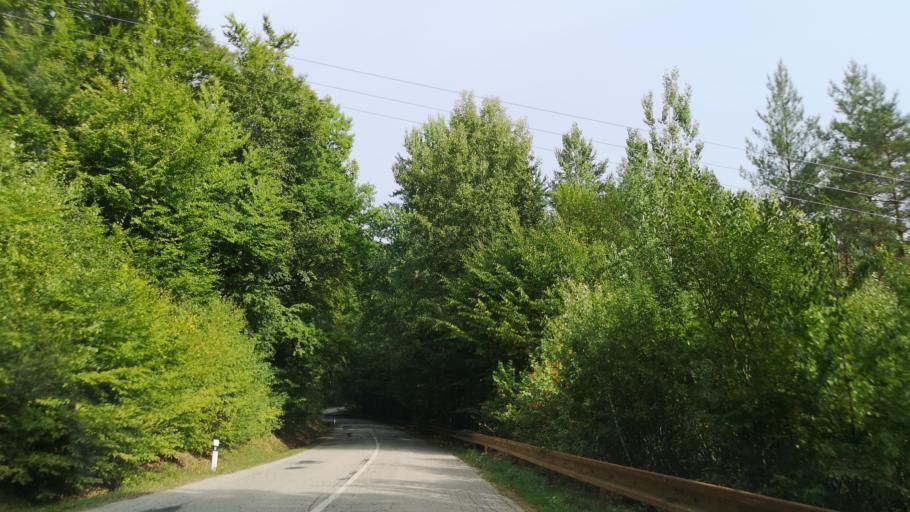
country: SK
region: Banskobystricky
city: Revuca
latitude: 48.6042
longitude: 20.1627
